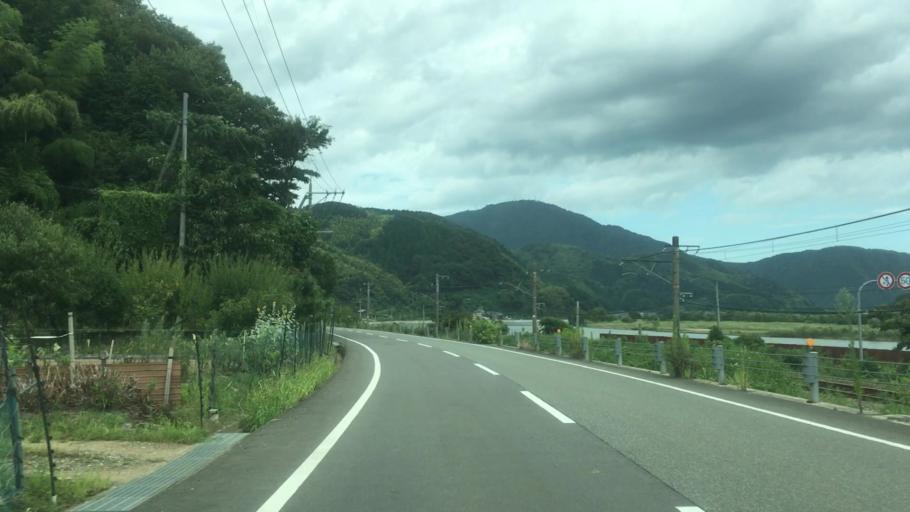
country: JP
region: Hyogo
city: Toyooka
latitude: 35.5751
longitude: 134.8045
